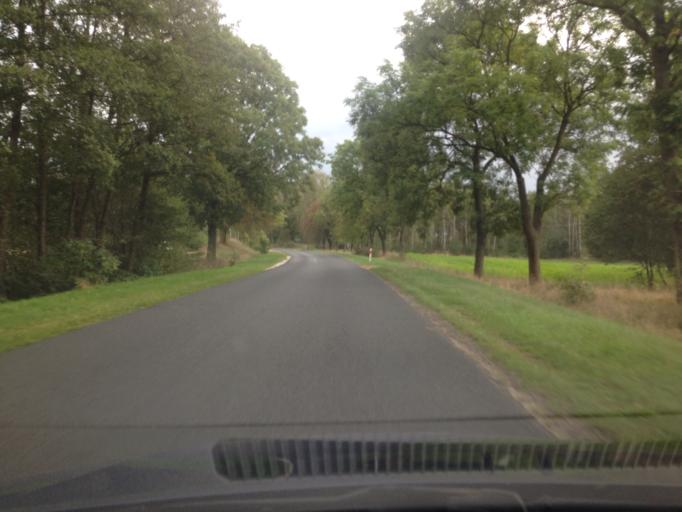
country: PL
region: Kujawsko-Pomorskie
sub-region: Powiat lipnowski
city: Lipno
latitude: 52.8019
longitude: 19.1951
